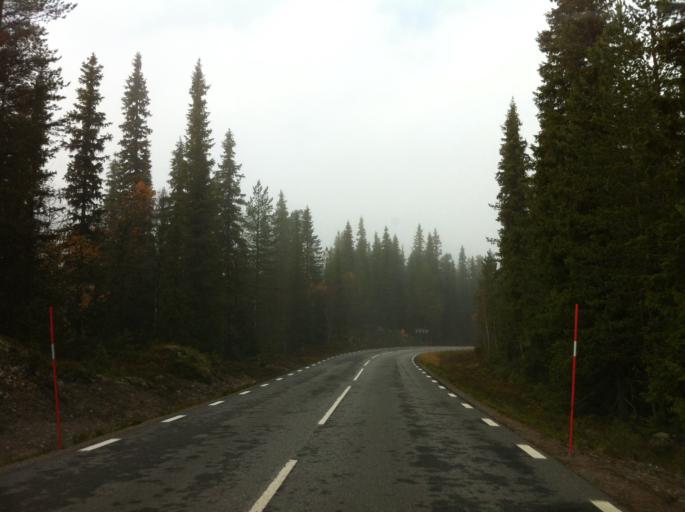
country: NO
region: Hedmark
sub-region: Engerdal
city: Engerdal
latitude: 61.9828
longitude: 12.4792
